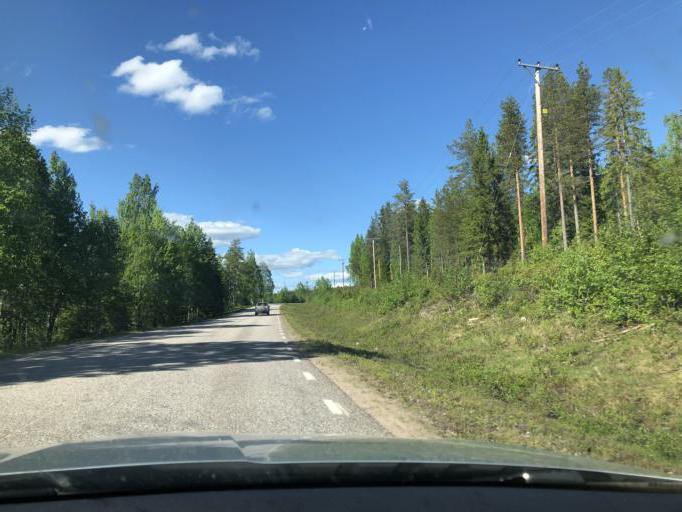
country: SE
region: Norrbotten
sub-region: Kalix Kommun
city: Kalix
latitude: 66.0149
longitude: 23.1415
